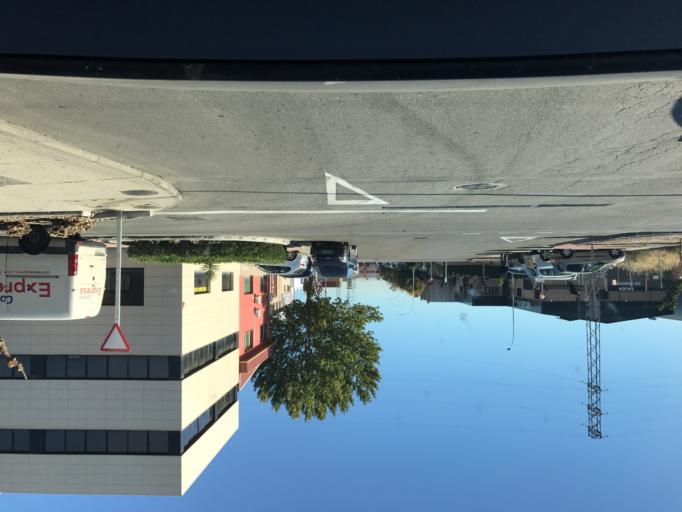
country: ES
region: Andalusia
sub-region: Provincia de Granada
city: Peligros
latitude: 37.2224
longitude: -3.6360
